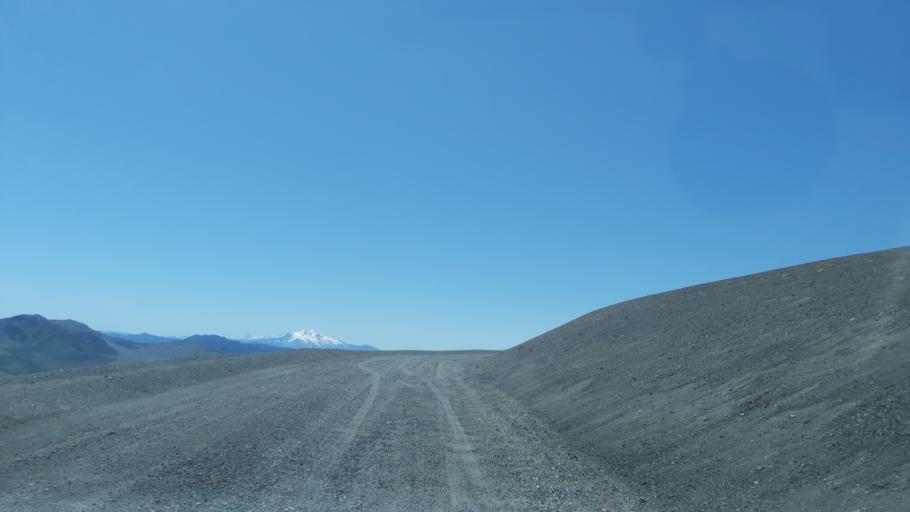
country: CL
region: Araucania
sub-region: Provincia de Cautin
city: Vilcun
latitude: -38.3678
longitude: -71.5398
